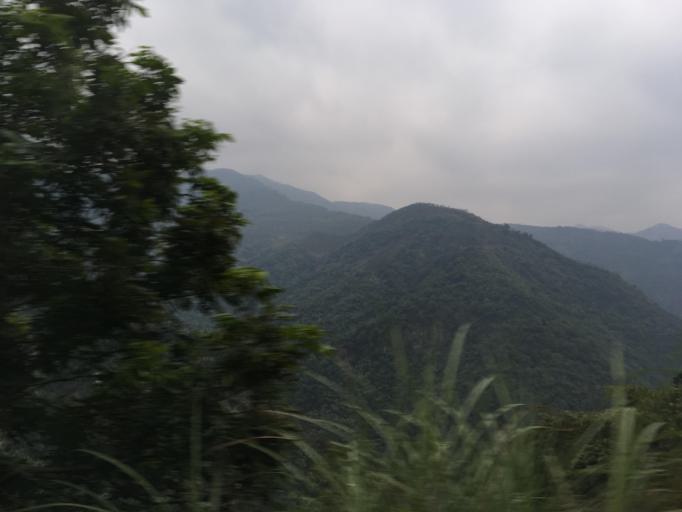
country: TW
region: Taiwan
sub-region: Chiayi
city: Jiayi Shi
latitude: 23.5370
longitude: 120.6097
